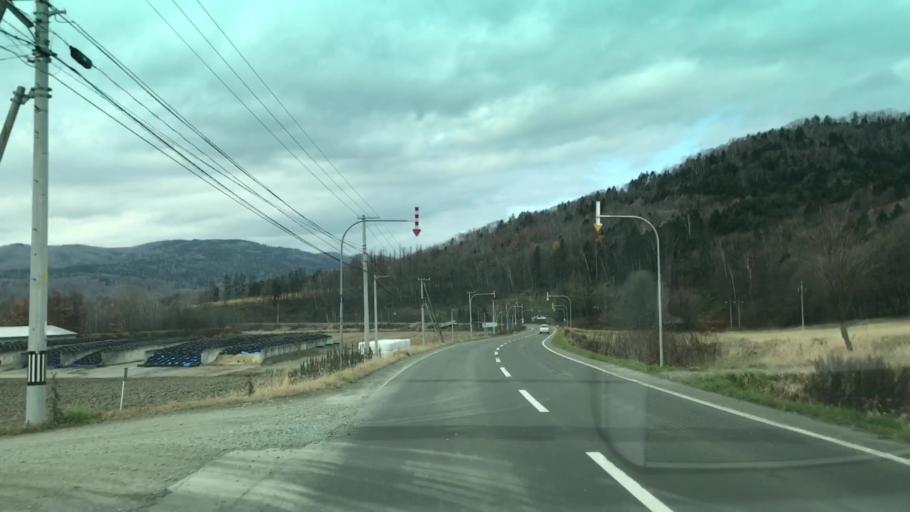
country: JP
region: Hokkaido
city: Shimo-furano
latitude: 42.9719
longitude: 142.4214
